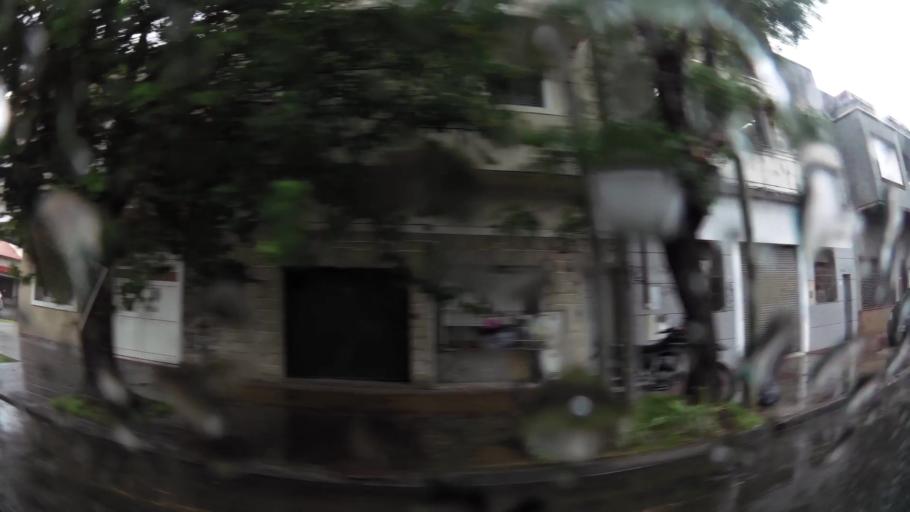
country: AR
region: Buenos Aires
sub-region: Partido de Lanus
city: Lanus
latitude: -34.7116
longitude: -58.3991
